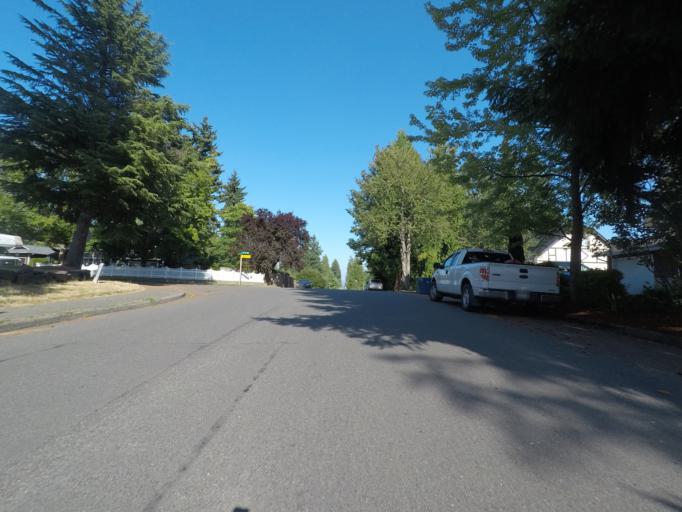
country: US
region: Washington
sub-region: King County
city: Inglewood-Finn Hill
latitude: 47.7334
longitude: -122.2368
